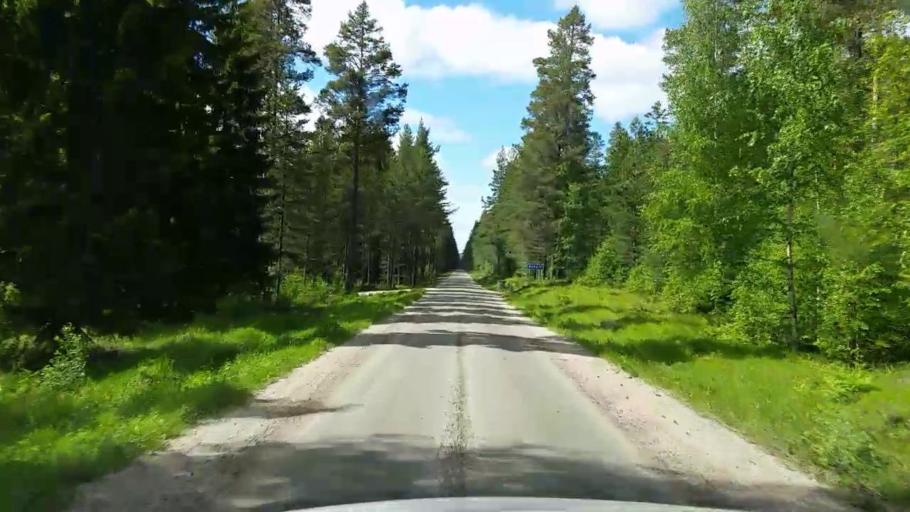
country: SE
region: Gaevleborg
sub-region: Ovanakers Kommun
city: Edsbyn
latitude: 61.5614
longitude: 15.9688
